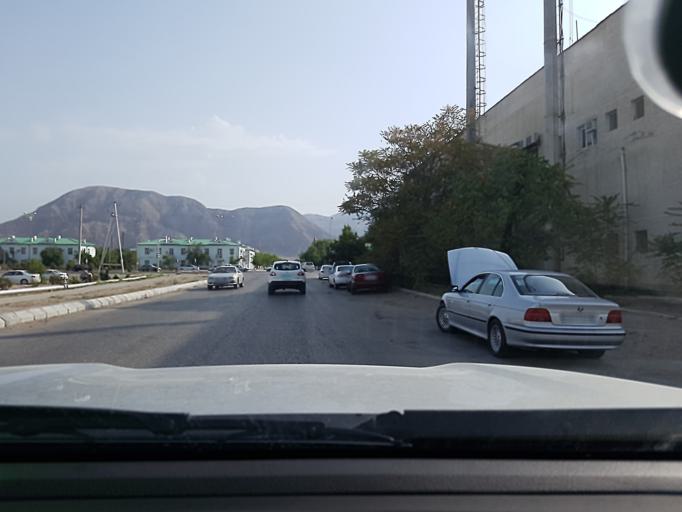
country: TM
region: Balkan
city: Balkanabat
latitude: 39.5044
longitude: 54.3547
